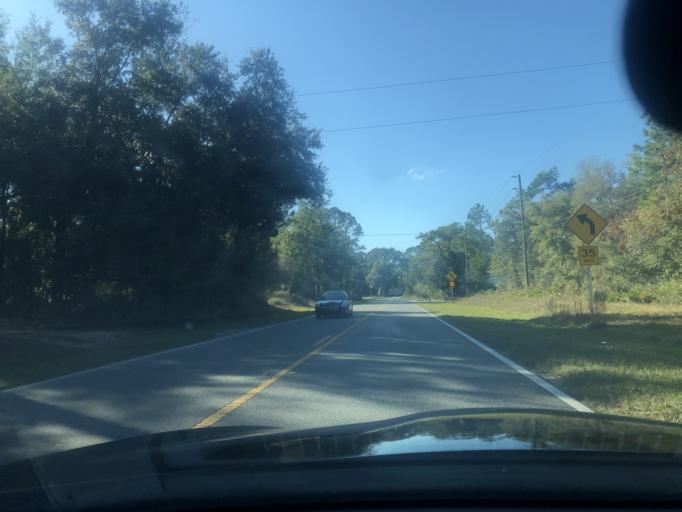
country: US
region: Florida
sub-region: Citrus County
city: Homosassa Springs
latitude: 28.8184
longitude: -82.5574
